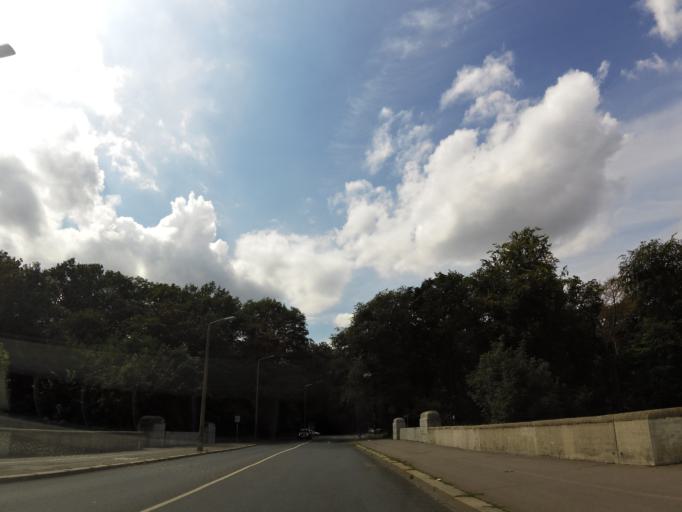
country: DE
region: Saxony
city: Leipzig
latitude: 51.3504
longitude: 12.3406
